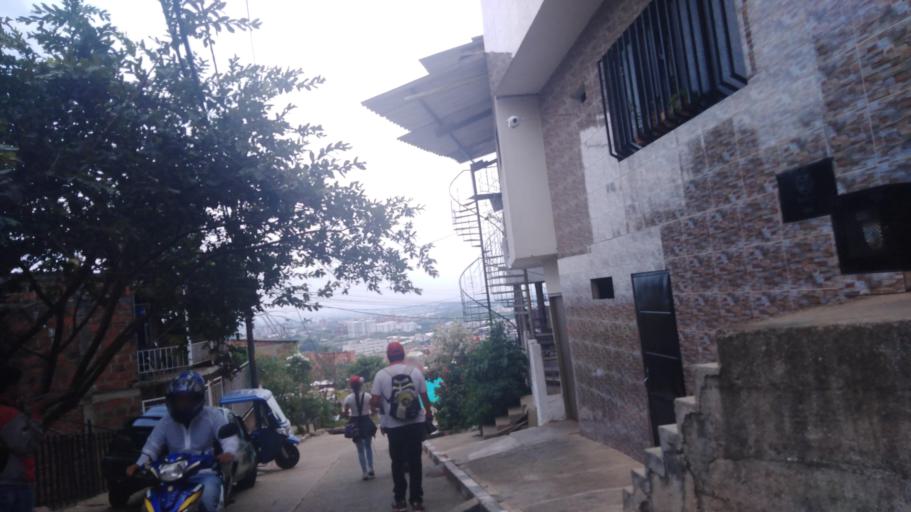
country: CO
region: Valle del Cauca
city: Cali
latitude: 3.3729
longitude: -76.5536
